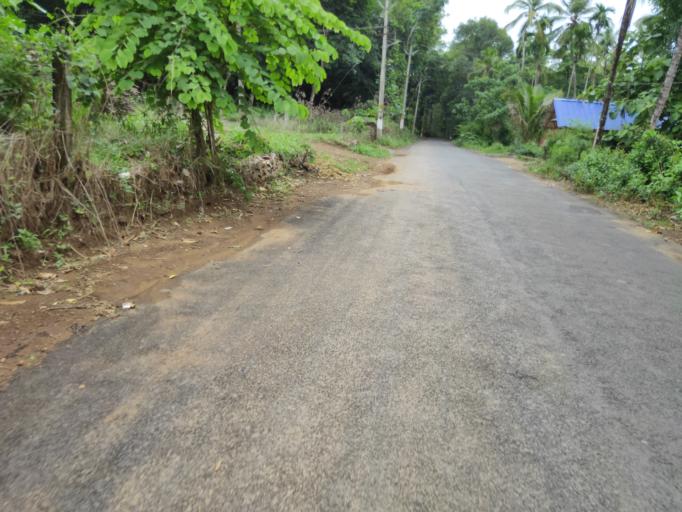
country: IN
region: Kerala
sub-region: Malappuram
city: Manjeri
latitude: 11.2411
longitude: 76.2464
